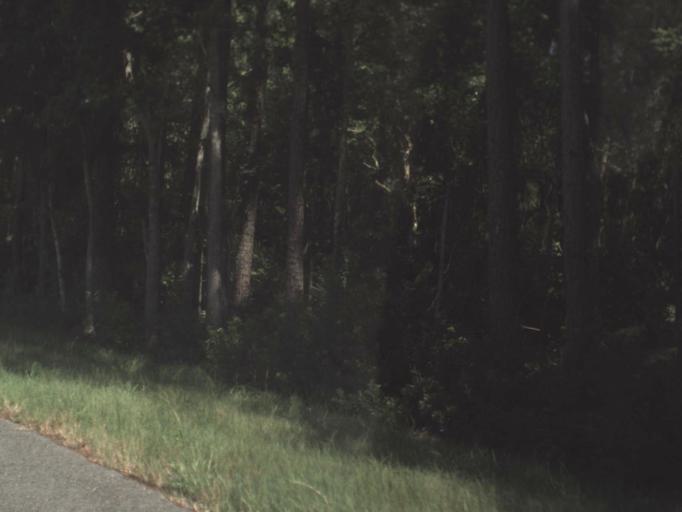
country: US
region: Florida
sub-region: Clay County
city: Green Cove Springs
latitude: 30.0362
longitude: -81.6534
